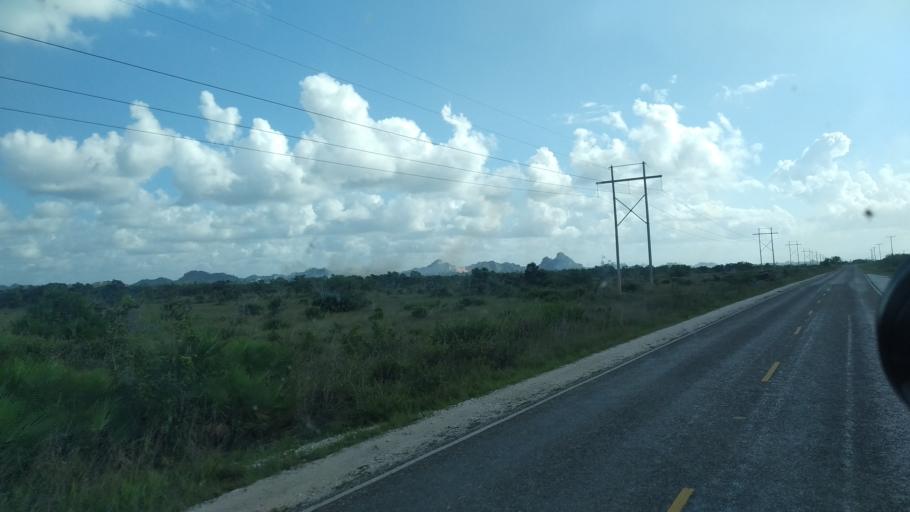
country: BZ
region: Belize
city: Belize City
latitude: 17.4222
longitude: -88.4394
